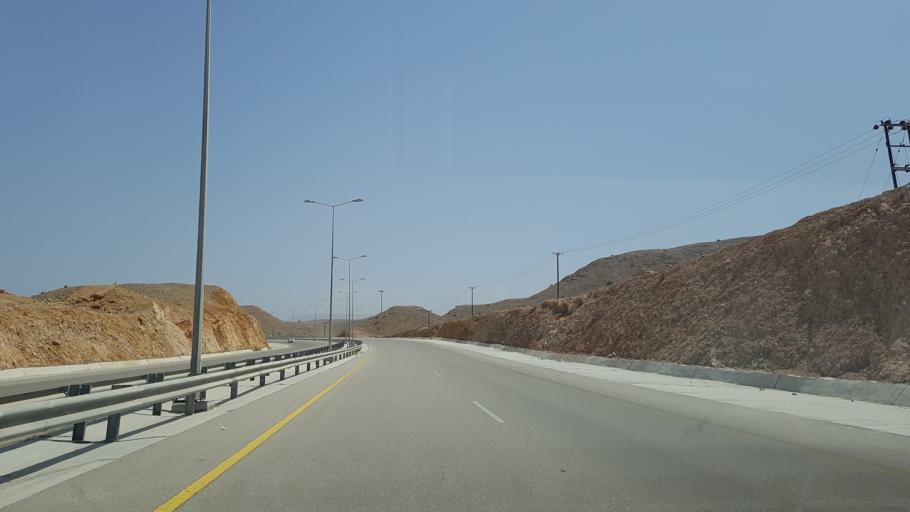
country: OM
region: Muhafazat Masqat
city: Muscat
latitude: 23.1334
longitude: 58.9721
